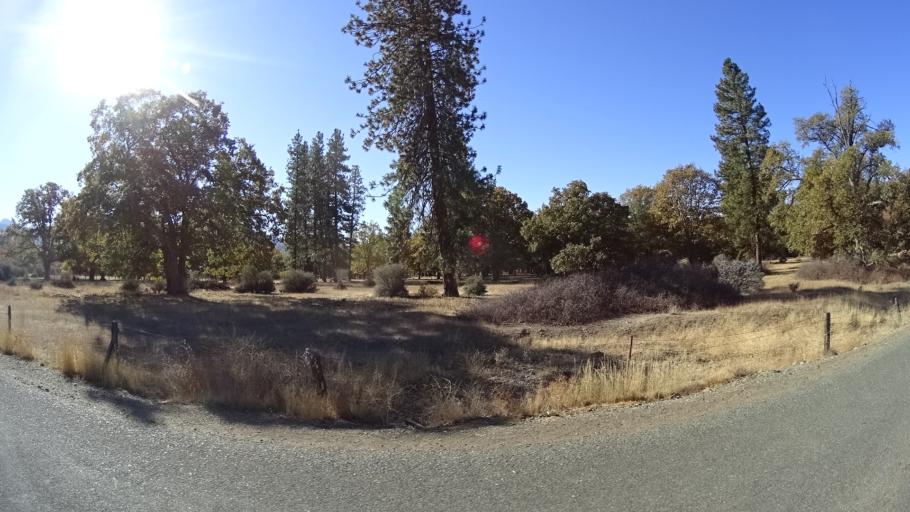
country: US
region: California
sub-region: Siskiyou County
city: Yreka
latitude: 41.5775
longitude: -122.8202
